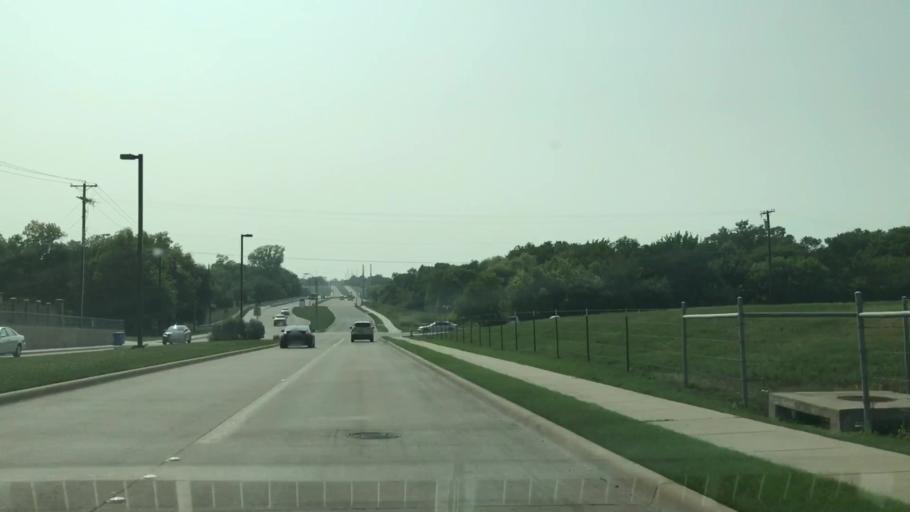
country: US
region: Texas
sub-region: Dallas County
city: Rowlett
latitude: 32.8940
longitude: -96.5862
